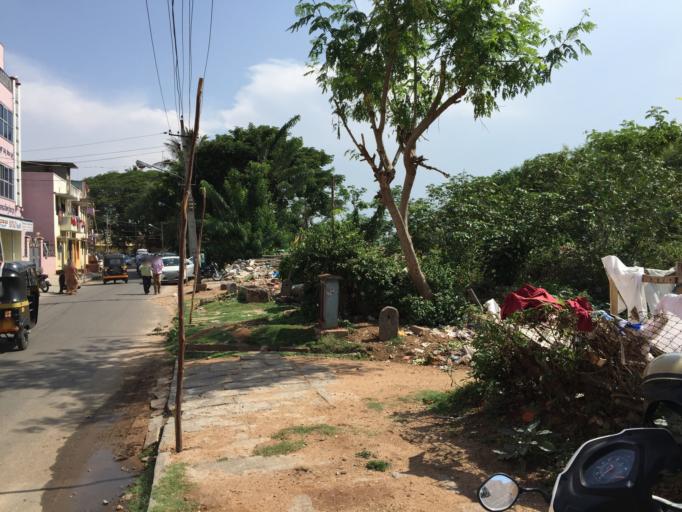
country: IN
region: Karnataka
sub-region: Mysore
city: Mysore
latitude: 12.2847
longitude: 76.6659
